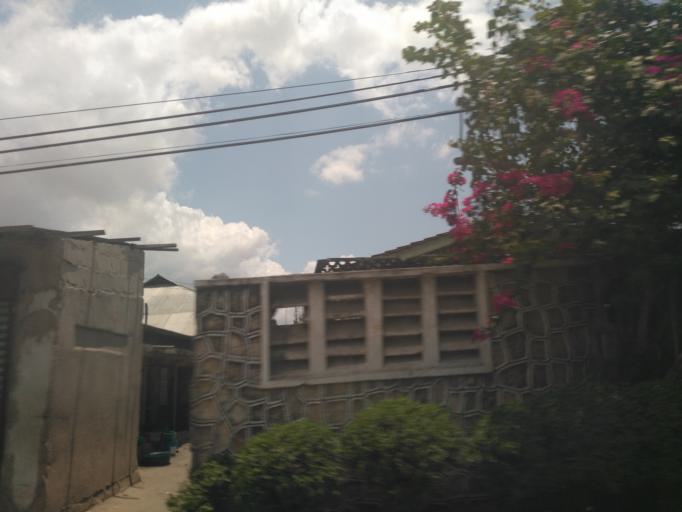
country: TZ
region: Dar es Salaam
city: Dar es Salaam
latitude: -6.8686
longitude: 39.2758
